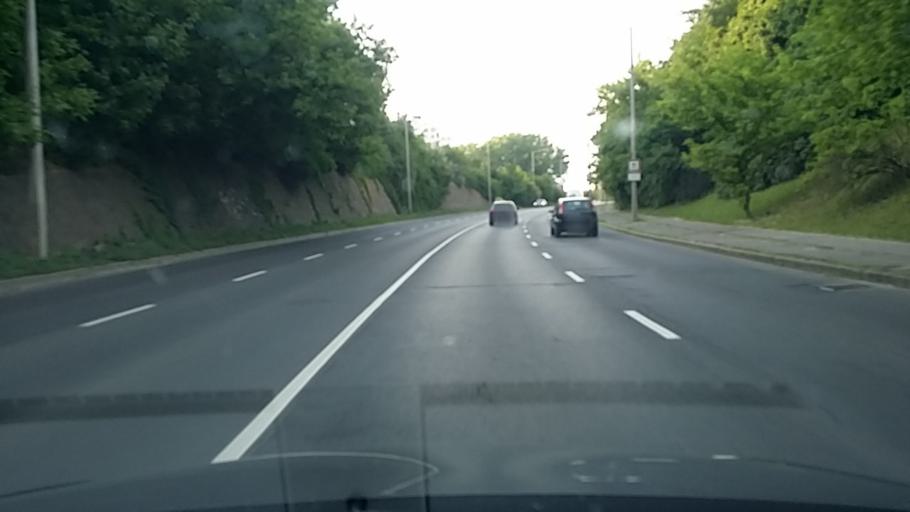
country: HU
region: Borsod-Abauj-Zemplen
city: Miskolc
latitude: 48.0786
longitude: 20.7842
